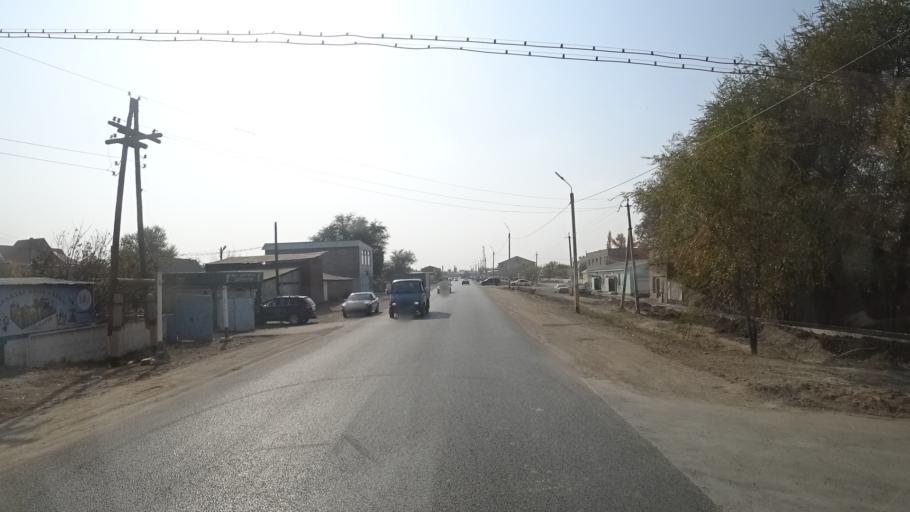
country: KZ
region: Zhambyl
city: Sarykemer
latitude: 43.0173
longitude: 71.5154
